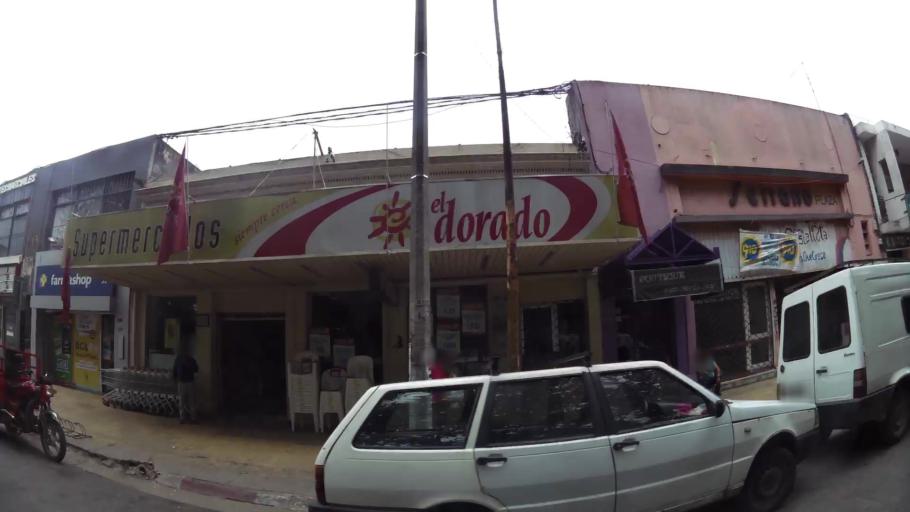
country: UY
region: Canelones
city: Las Piedras
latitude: -34.7279
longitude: -56.2164
